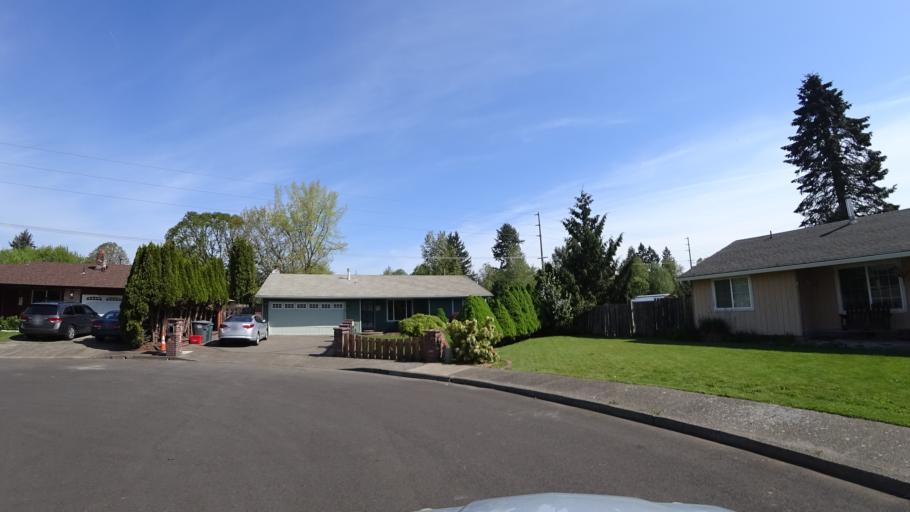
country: US
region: Oregon
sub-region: Washington County
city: Hillsboro
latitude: 45.5277
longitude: -122.9396
